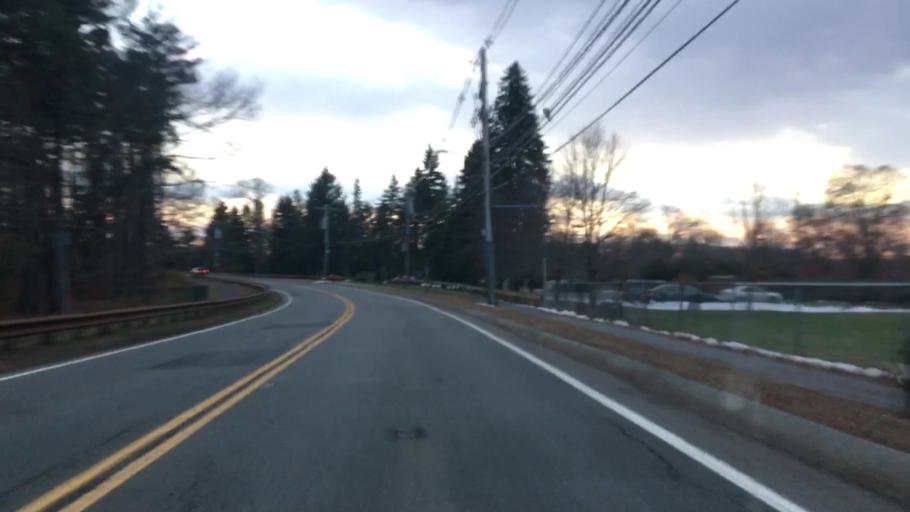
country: US
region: Massachusetts
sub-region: Middlesex County
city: Framingham Center
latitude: 42.2837
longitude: -71.4338
